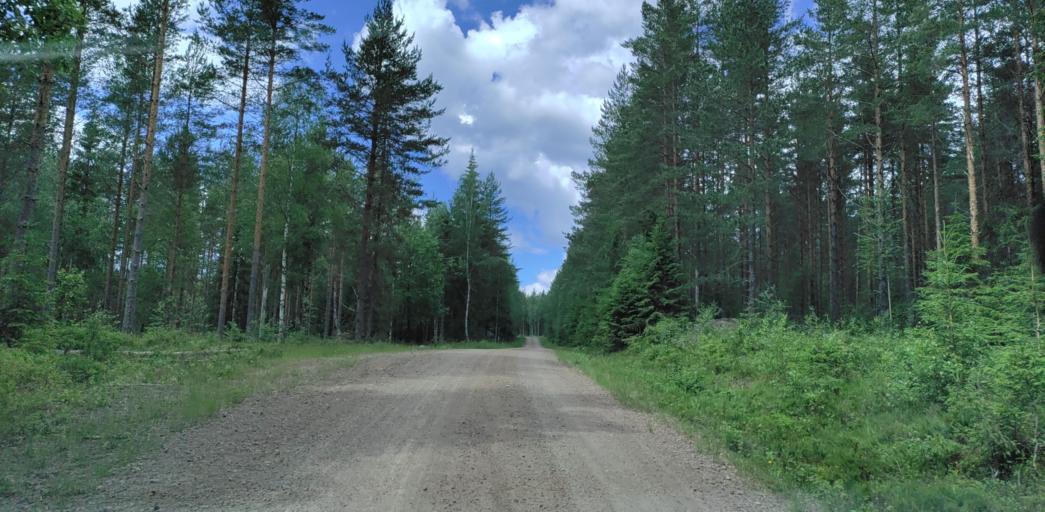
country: SE
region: Vaermland
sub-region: Hagfors Kommun
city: Ekshaerad
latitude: 60.0910
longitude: 13.4109
